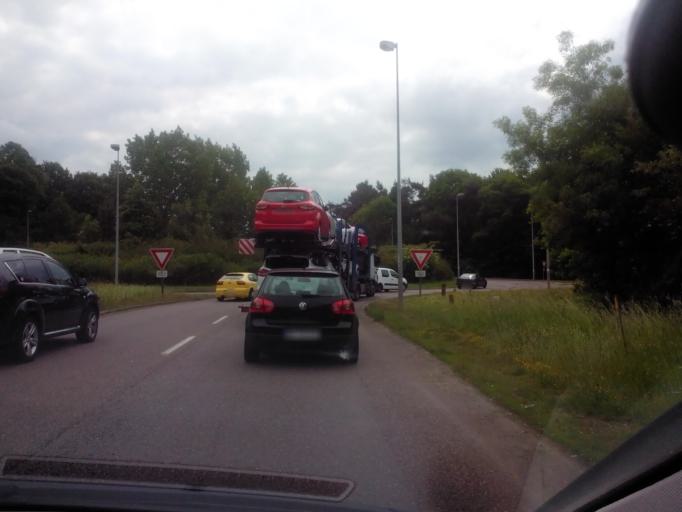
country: FR
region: Lorraine
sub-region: Departement de la Moselle
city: Carling
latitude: 49.1416
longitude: 6.7076
